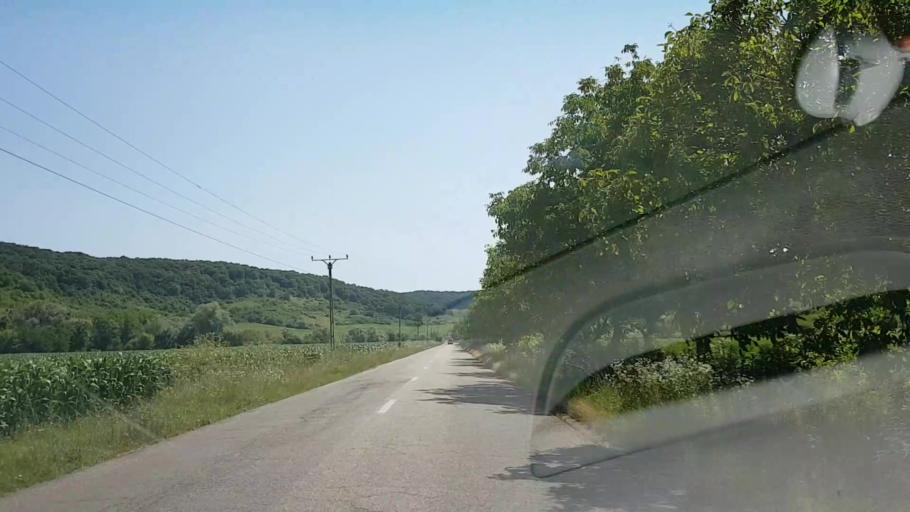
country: RO
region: Mures
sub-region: Comuna Apold
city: Apold
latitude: 46.1426
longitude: 24.8029
